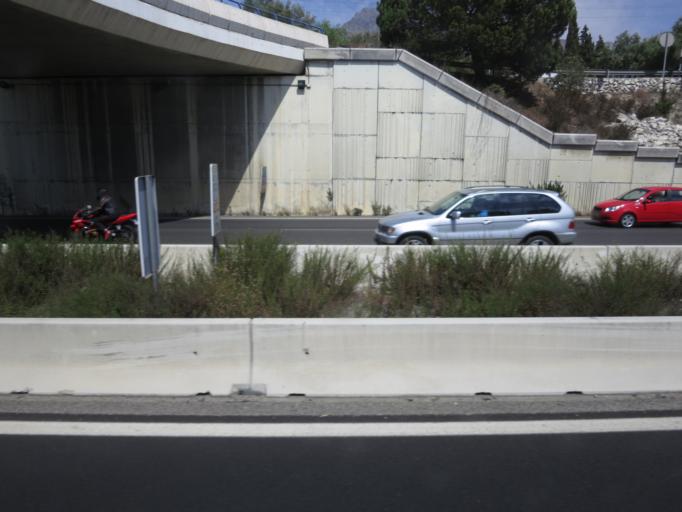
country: ES
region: Andalusia
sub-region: Provincia de Malaga
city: Marbella
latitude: 36.5129
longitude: -4.9256
